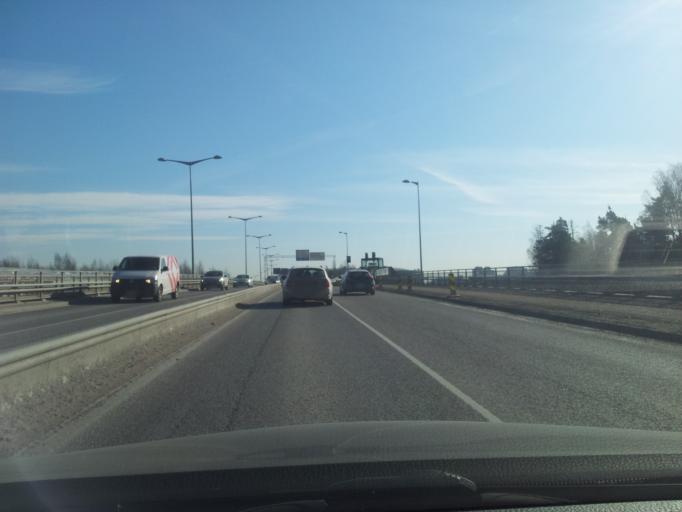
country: FI
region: Uusimaa
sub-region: Helsinki
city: Helsinki
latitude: 60.2080
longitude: 24.9193
